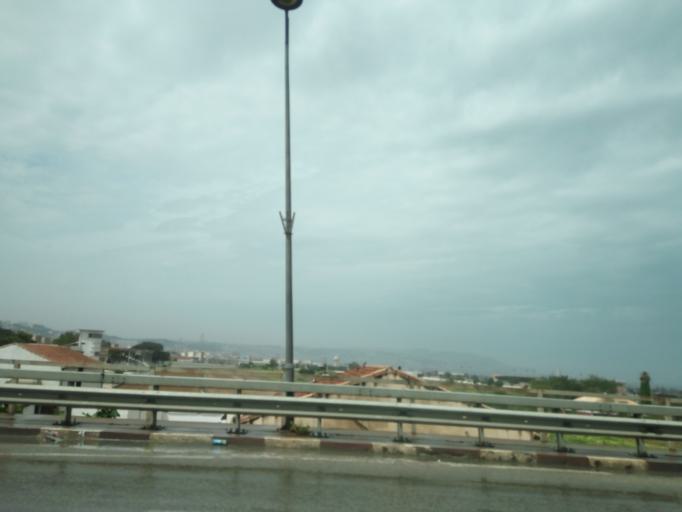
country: DZ
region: Alger
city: Bab Ezzouar
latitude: 36.7366
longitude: 3.1214
